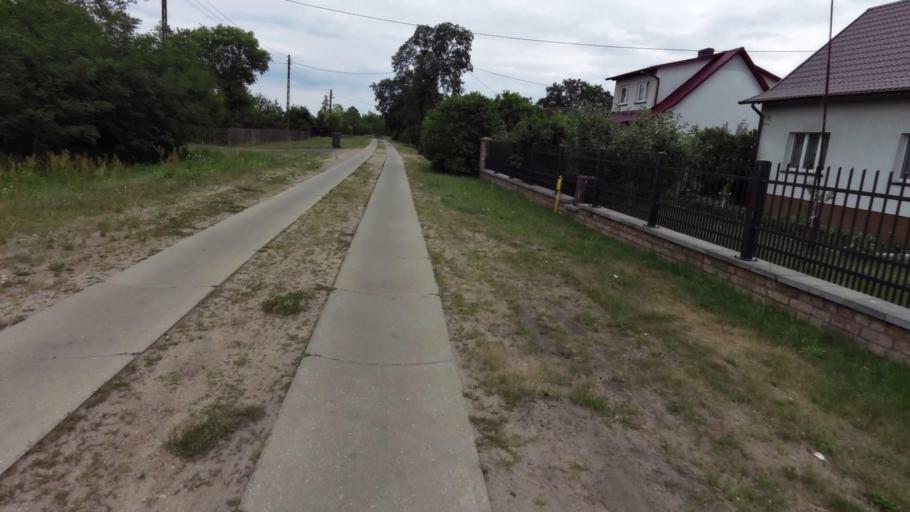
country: PL
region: Lubusz
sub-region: Powiat gorzowski
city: Kostrzyn nad Odra
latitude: 52.6203
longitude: 14.5884
